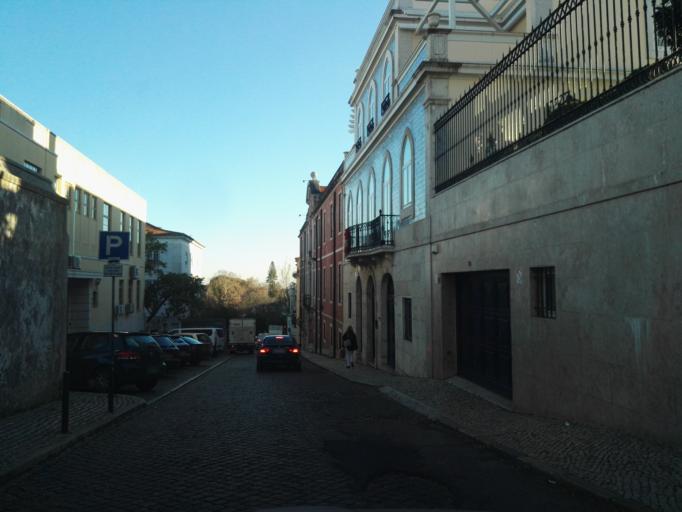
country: PT
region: Lisbon
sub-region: Lisbon
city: Lisbon
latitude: 38.7162
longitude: -9.1615
